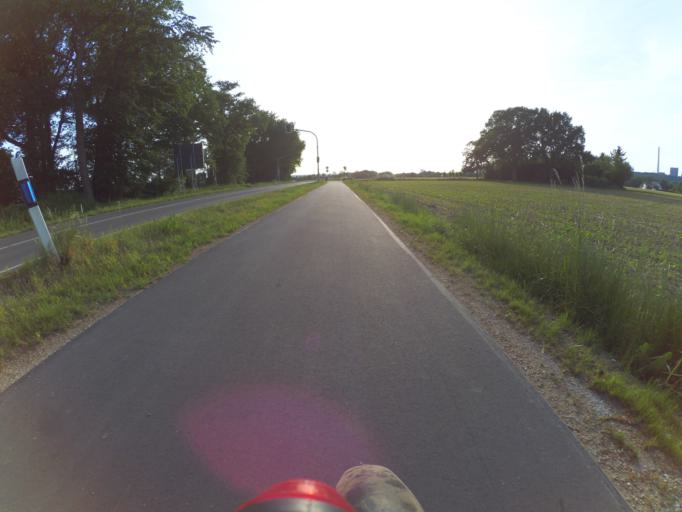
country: DE
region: North Rhine-Westphalia
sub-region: Regierungsbezirk Munster
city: Mettingen
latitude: 52.2611
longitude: 7.7706
